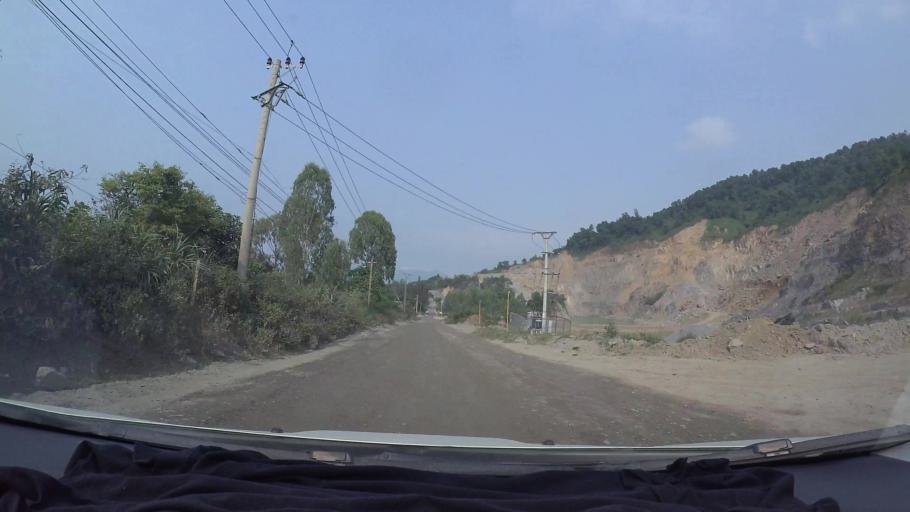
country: VN
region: Da Nang
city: Lien Chieu
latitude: 16.0382
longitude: 108.1562
